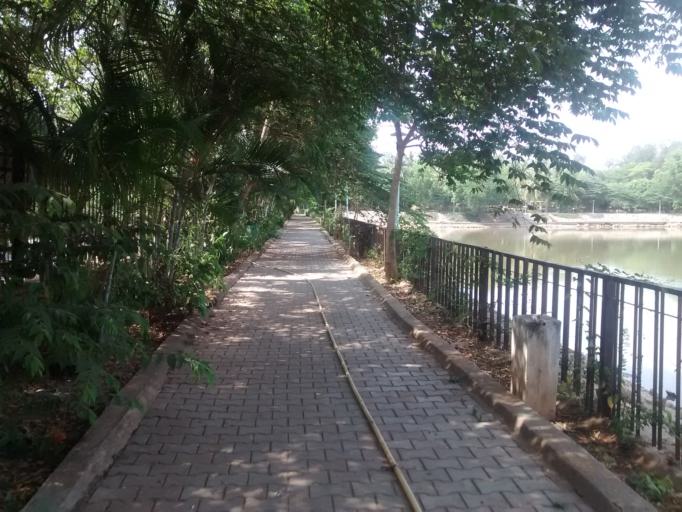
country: IN
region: Karnataka
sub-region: Dharwad
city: Hubli
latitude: 15.4639
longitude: 74.9858
